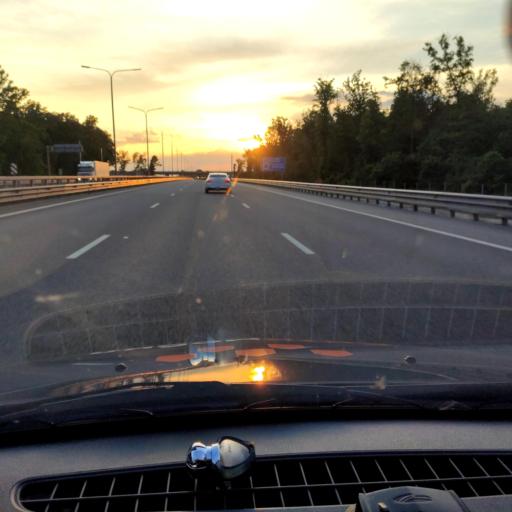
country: RU
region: Voronezj
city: Podgornoye
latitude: 51.8365
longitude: 39.2265
